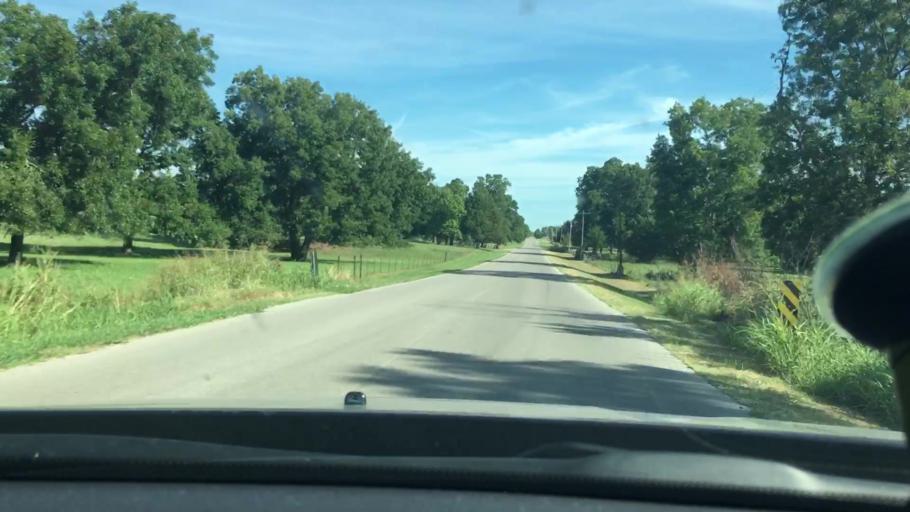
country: US
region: Oklahoma
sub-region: Carter County
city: Lone Grove
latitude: 34.2386
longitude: -97.2474
